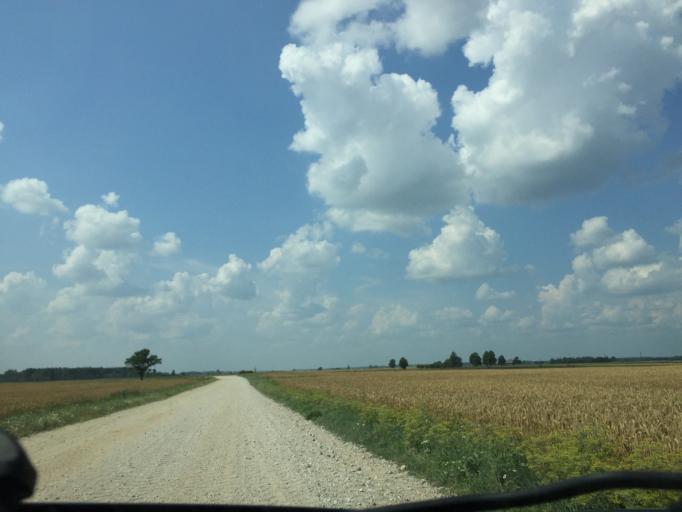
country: LT
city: Zagare
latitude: 56.3955
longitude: 23.2145
